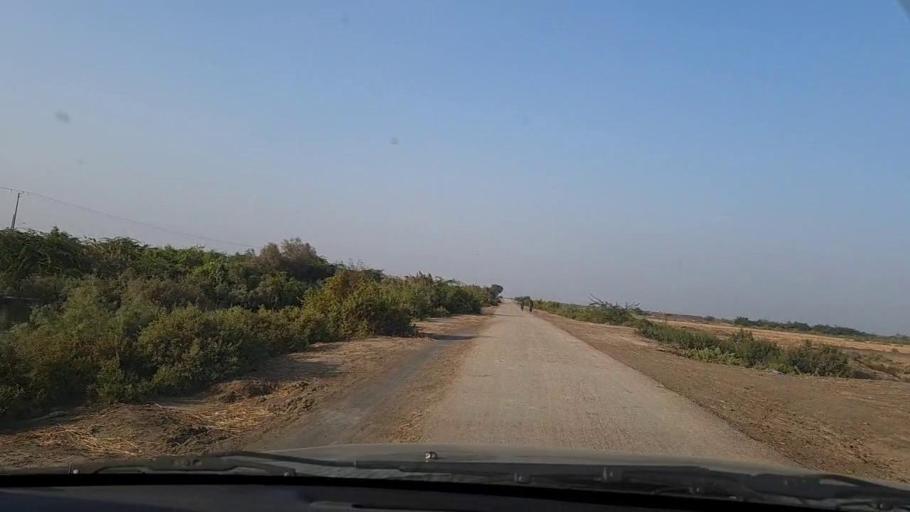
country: PK
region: Sindh
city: Chuhar Jamali
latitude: 24.3037
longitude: 67.7555
